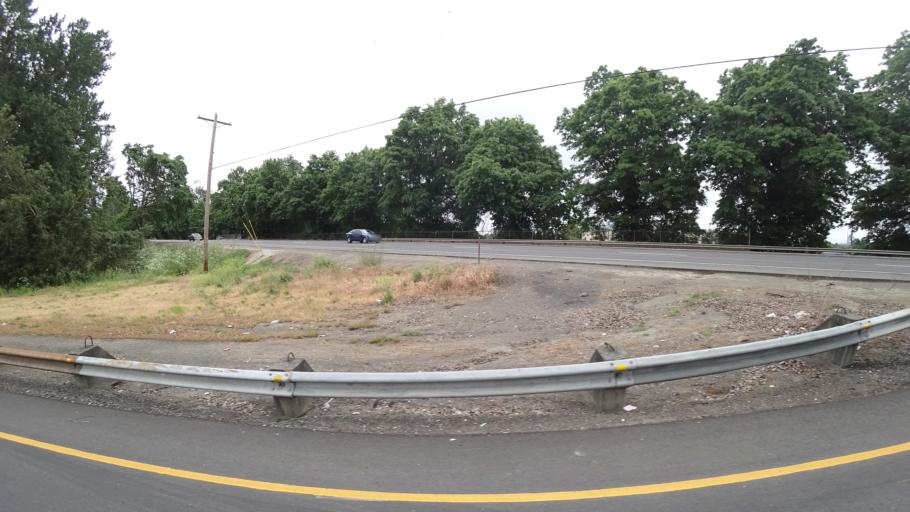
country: US
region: Washington
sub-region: Clark County
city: Vancouver
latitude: 45.5963
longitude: -122.6712
